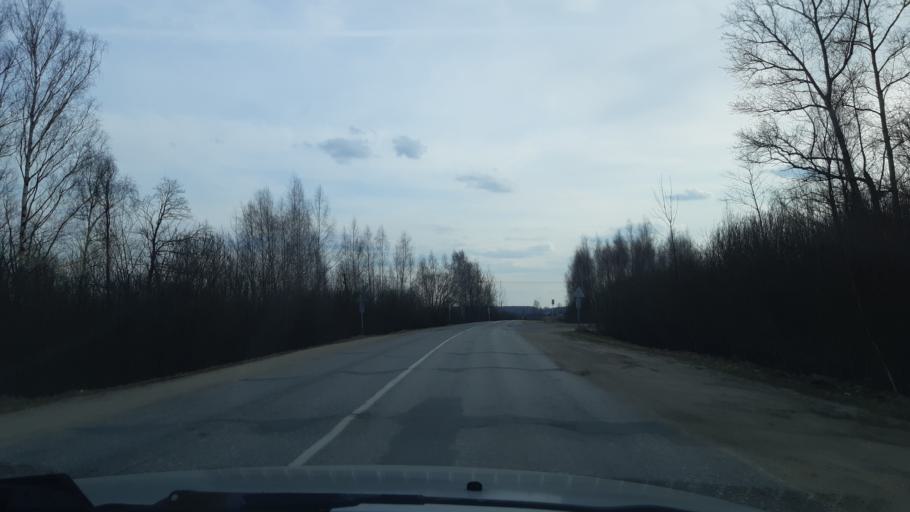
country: RU
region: Vladimir
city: Luknovo
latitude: 56.2223
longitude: 42.0344
